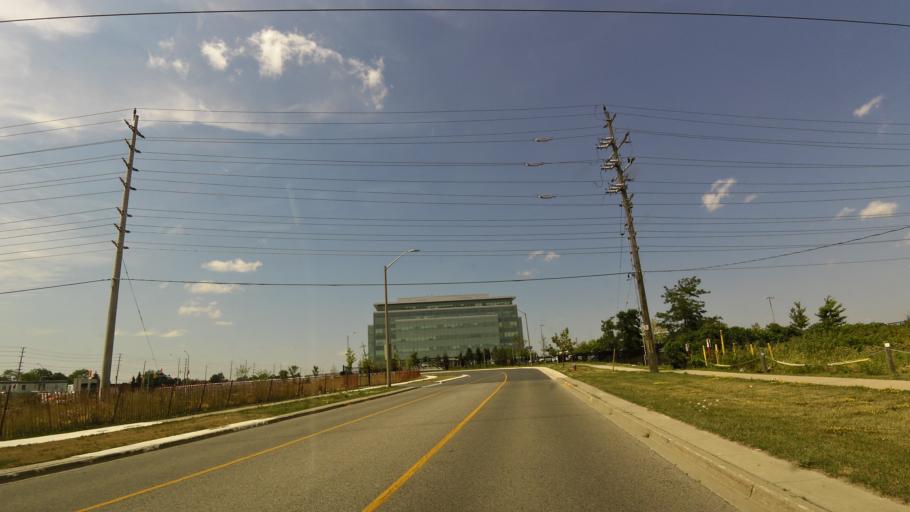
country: CA
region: Ontario
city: Etobicoke
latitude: 43.6371
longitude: -79.6069
